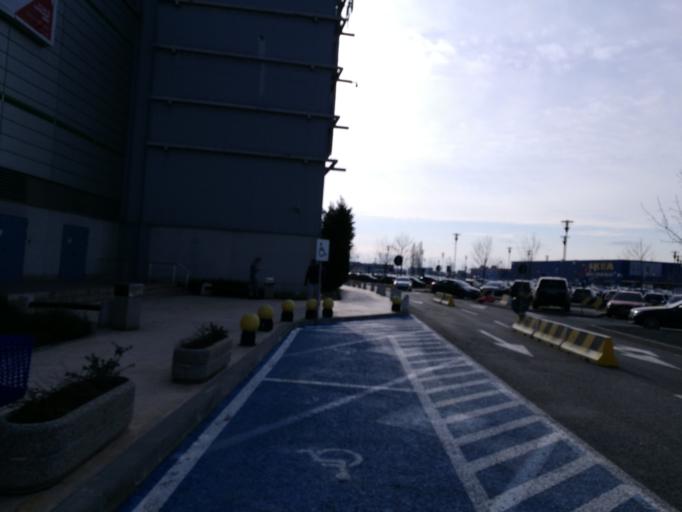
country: RO
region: Ilfov
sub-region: Comuna Otopeni
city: Otopeni
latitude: 44.5077
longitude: 26.0891
